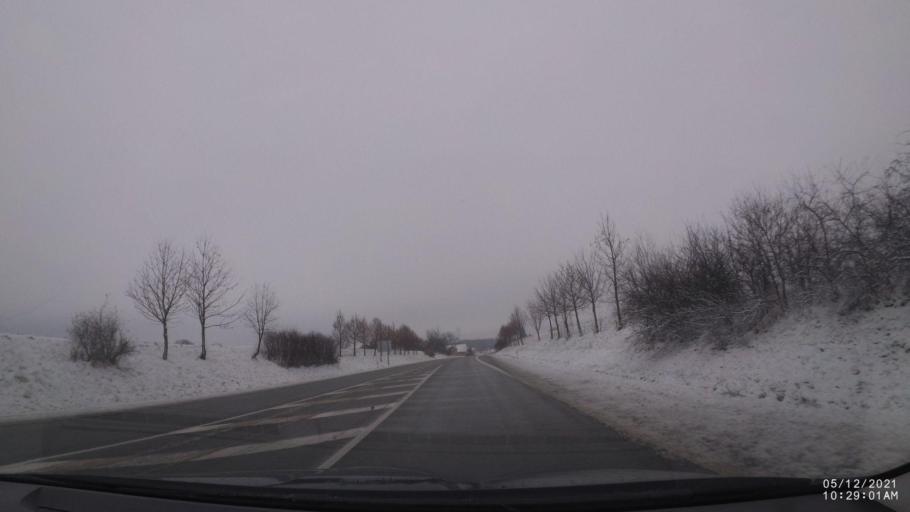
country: CZ
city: Vamberk
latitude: 50.1286
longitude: 16.2845
